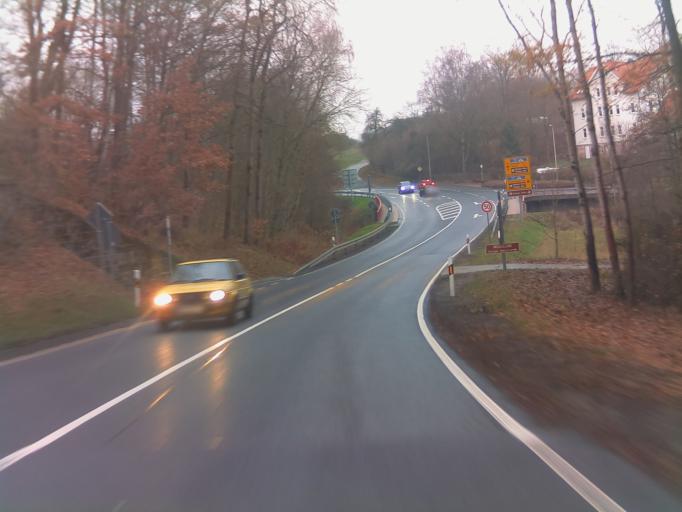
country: DE
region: Thuringia
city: Grimmelshausen
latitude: 50.4901
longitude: 10.6372
